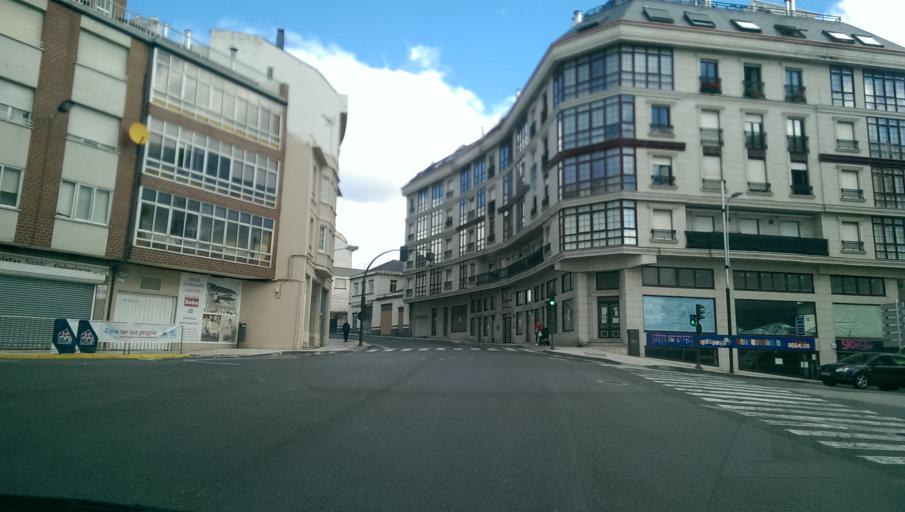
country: ES
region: Galicia
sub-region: Provincia de Lugo
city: Foz
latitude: 43.5692
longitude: -7.2581
